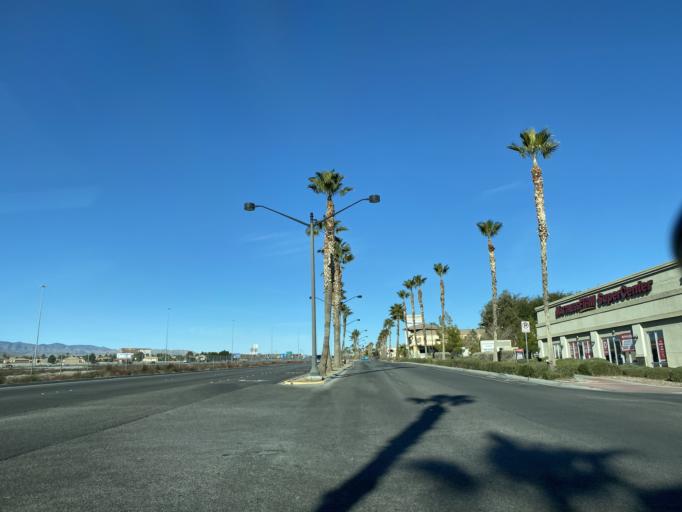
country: US
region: Nevada
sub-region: Clark County
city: Las Vegas
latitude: 36.2810
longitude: -115.2675
